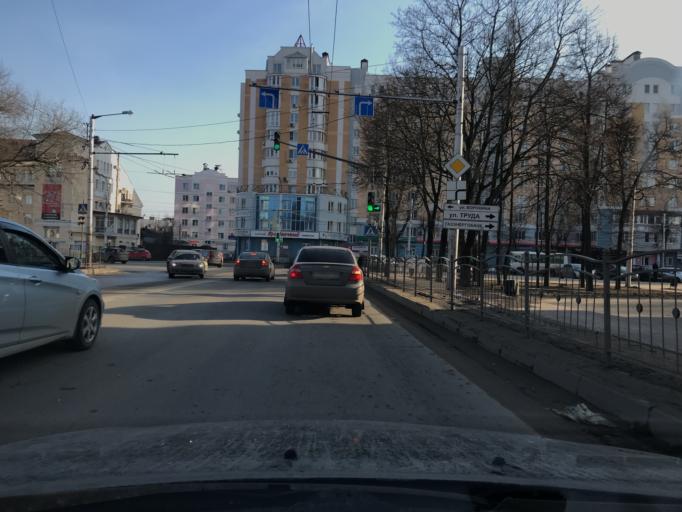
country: RU
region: Kaluga
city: Kaluga
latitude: 54.5216
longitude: 36.2599
